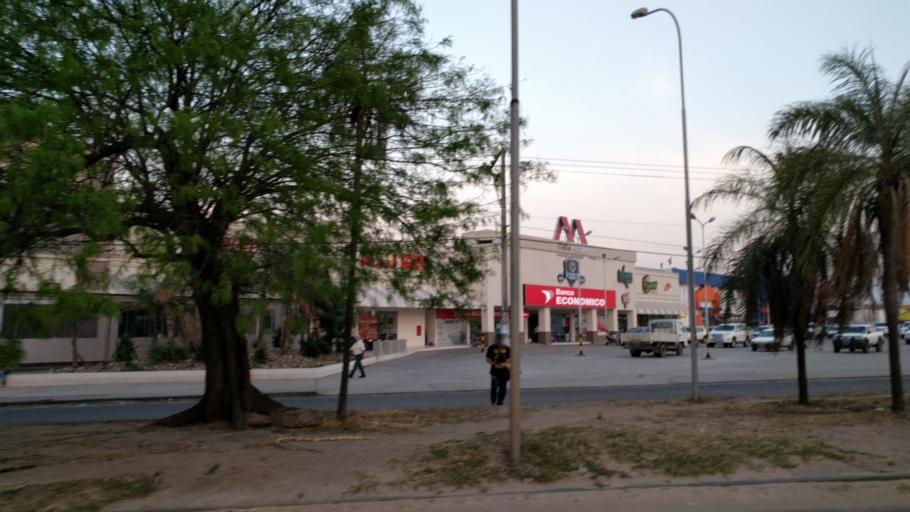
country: BO
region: Santa Cruz
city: Santa Cruz de la Sierra
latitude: -17.7641
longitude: -63.1481
